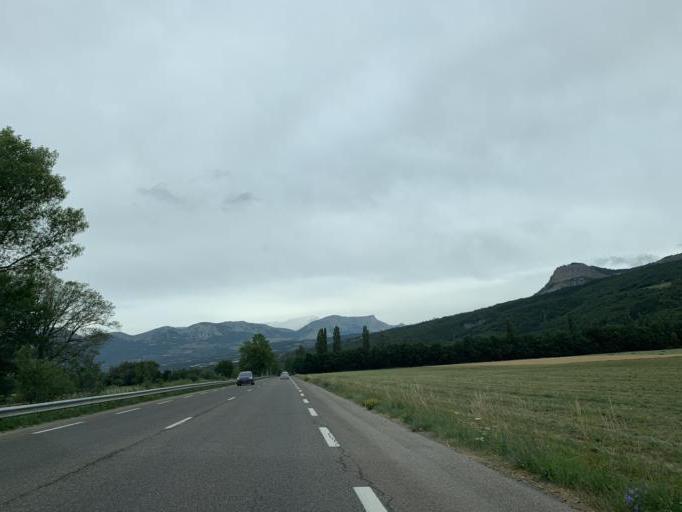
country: FR
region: Provence-Alpes-Cote d'Azur
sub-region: Departement des Hautes-Alpes
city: La Batie-Neuve
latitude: 44.5716
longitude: 6.1775
